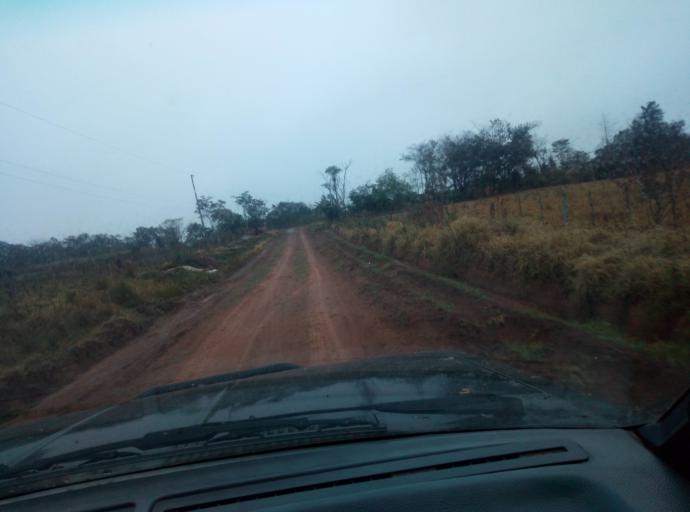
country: PY
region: Caaguazu
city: Carayao
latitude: -25.1904
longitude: -56.3179
